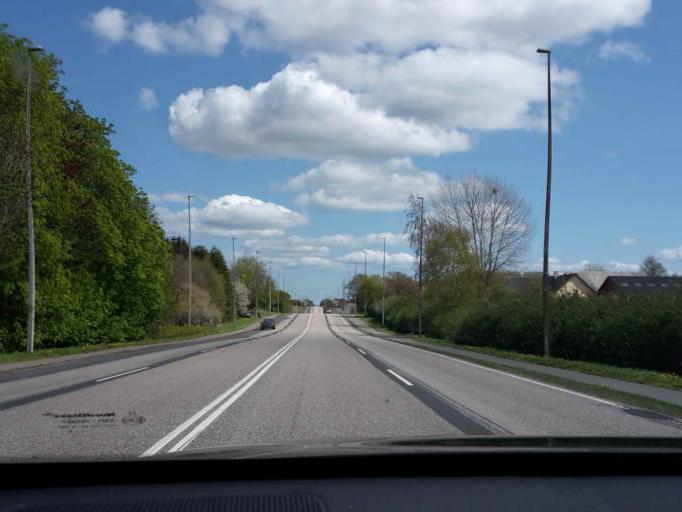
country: DK
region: South Denmark
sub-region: Odense Kommune
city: Bellinge
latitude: 55.3911
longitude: 10.2853
